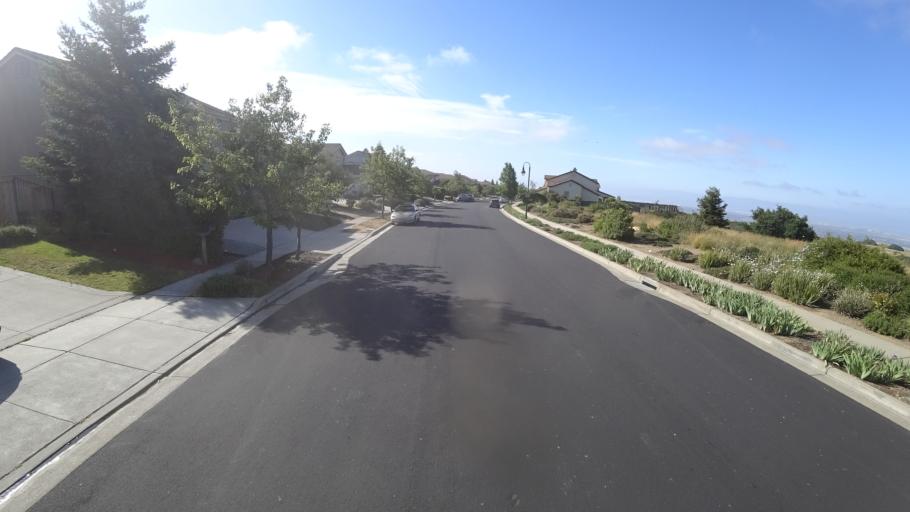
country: US
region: California
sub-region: Alameda County
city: Fairview
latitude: 37.6512
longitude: -122.0197
